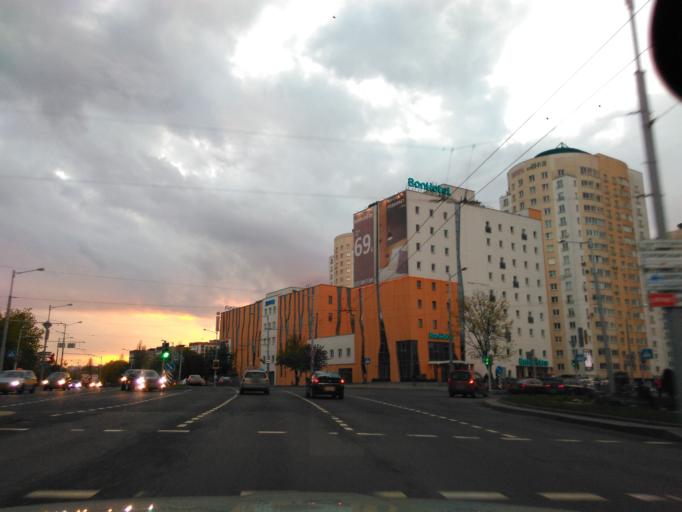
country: BY
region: Minsk
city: Minsk
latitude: 53.9098
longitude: 27.5074
